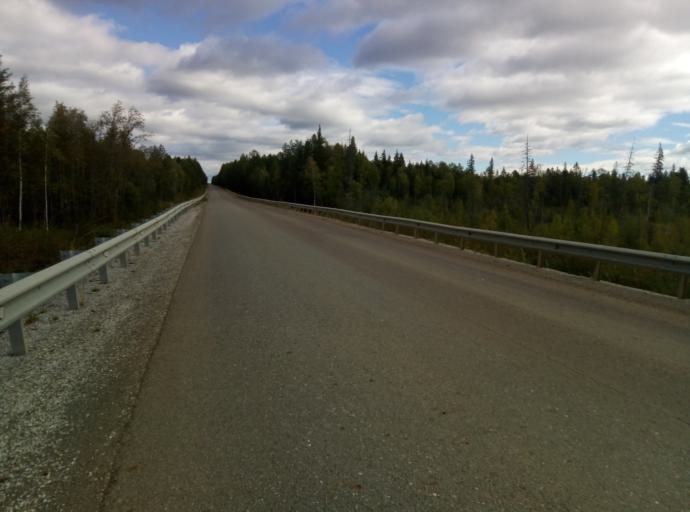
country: RU
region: Sverdlovsk
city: Karpinsk
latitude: 59.7004
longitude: 59.8888
